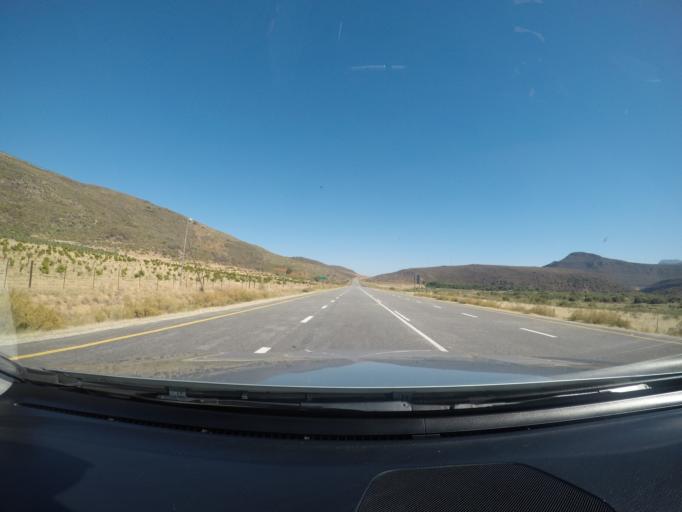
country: ZA
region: Western Cape
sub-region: West Coast District Municipality
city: Clanwilliam
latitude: -32.3819
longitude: 18.9455
